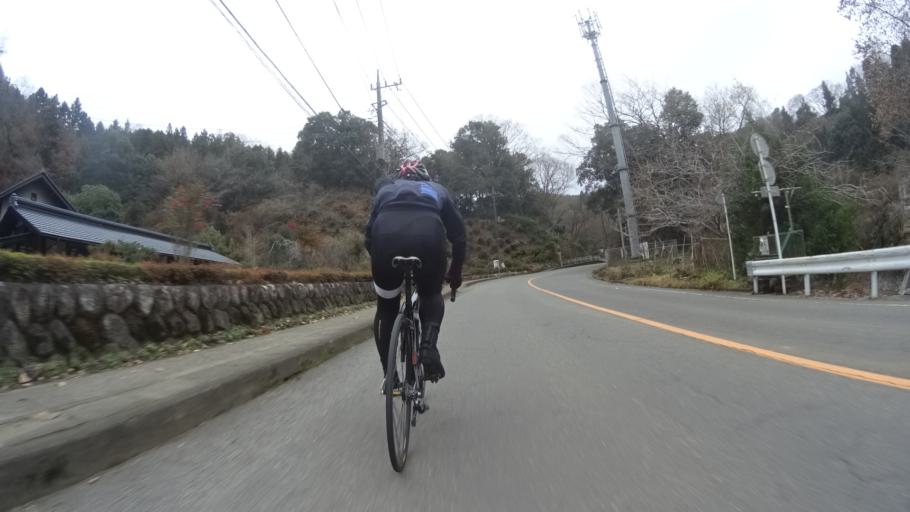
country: JP
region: Yamanashi
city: Uenohara
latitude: 35.6286
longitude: 139.1494
